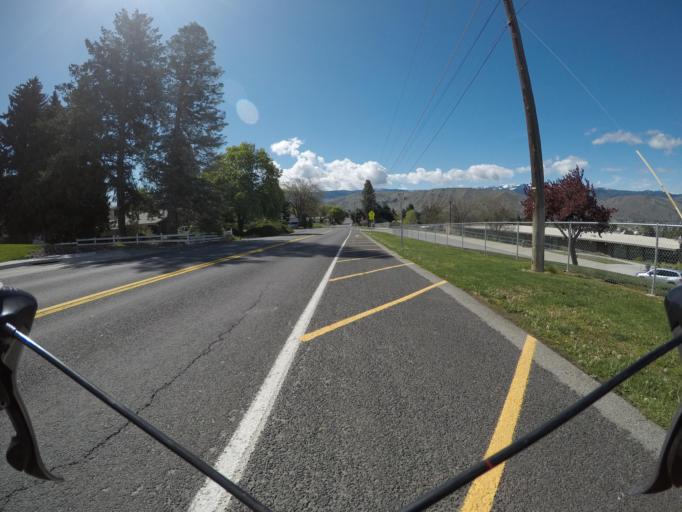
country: US
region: Washington
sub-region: Douglas County
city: East Wenatchee Bench
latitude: 47.4145
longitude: -120.2693
